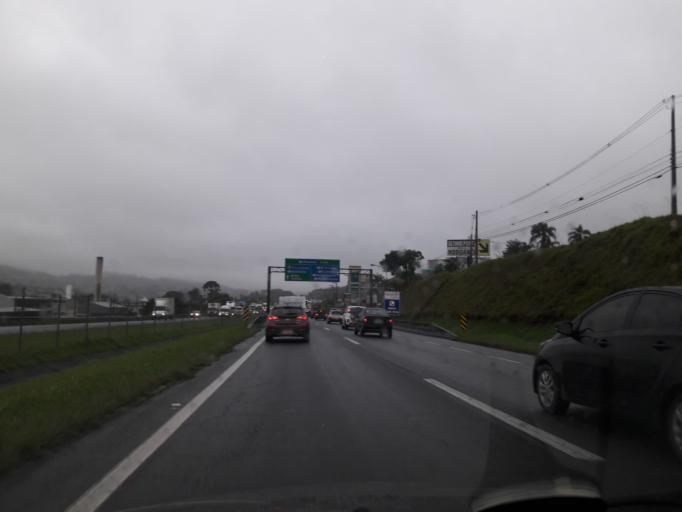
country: BR
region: Sao Paulo
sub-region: Embu
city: Embu
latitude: -23.6656
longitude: -46.8544
